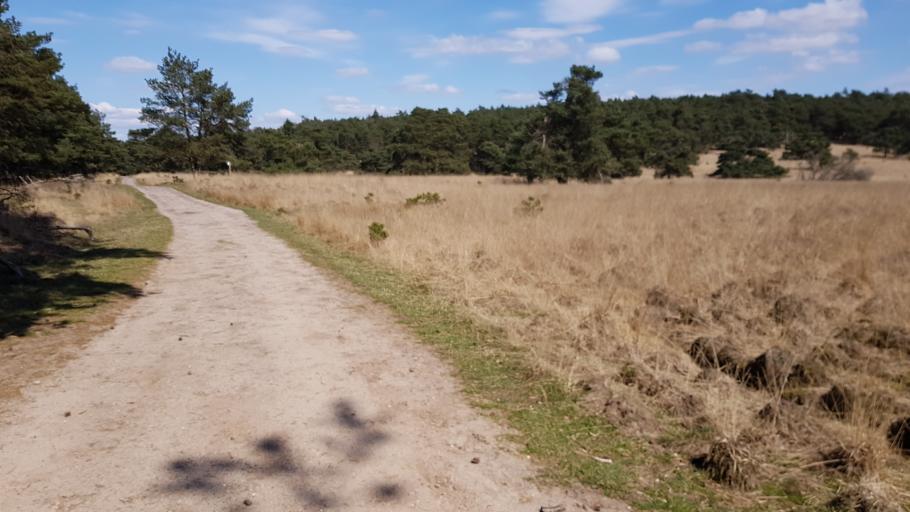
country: NL
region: Gelderland
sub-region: Gemeente Rheden
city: Rheden
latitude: 52.0571
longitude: 6.0043
